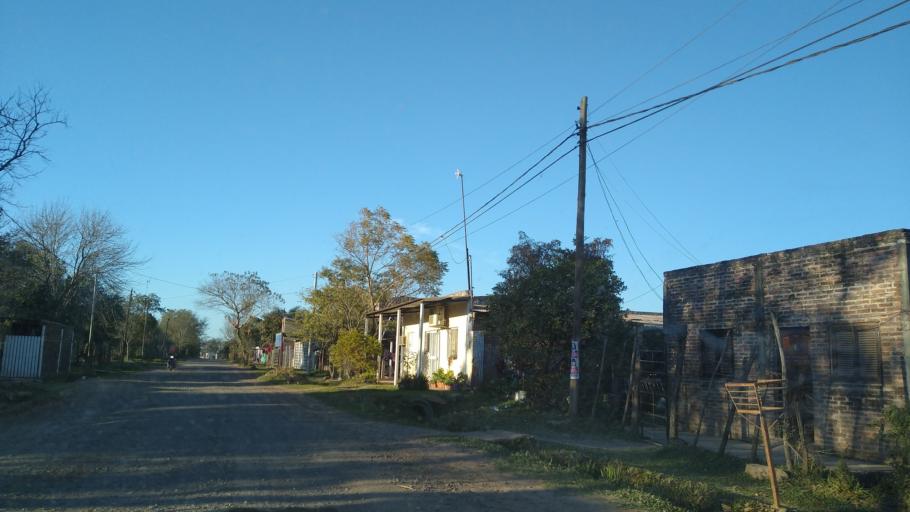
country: AR
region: Chaco
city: Barranqueras
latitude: -27.4719
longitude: -58.9480
